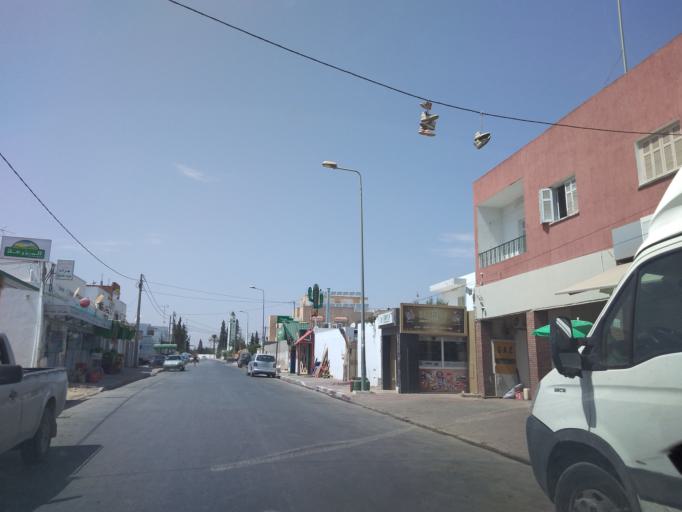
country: TN
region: Safaqis
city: Sfax
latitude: 34.7603
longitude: 10.7495
